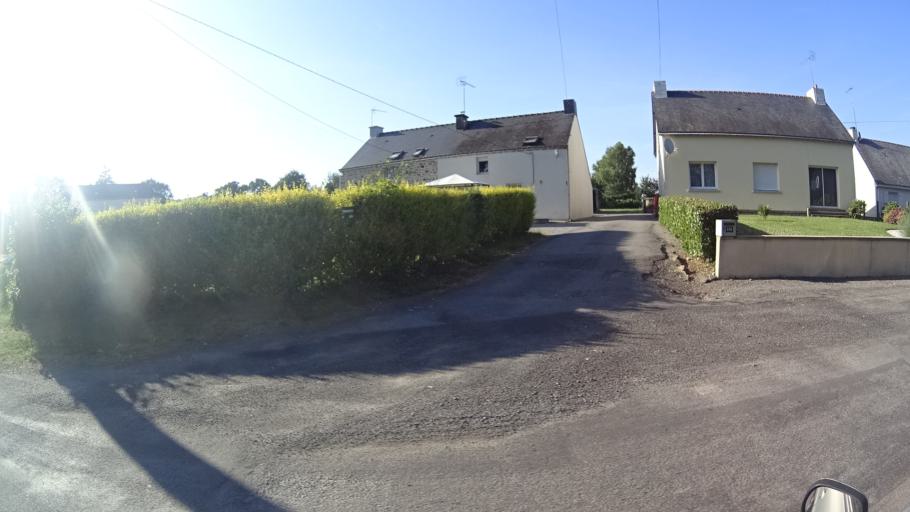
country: FR
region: Brittany
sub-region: Departement du Morbihan
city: Rieux
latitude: 47.6120
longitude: -2.1110
